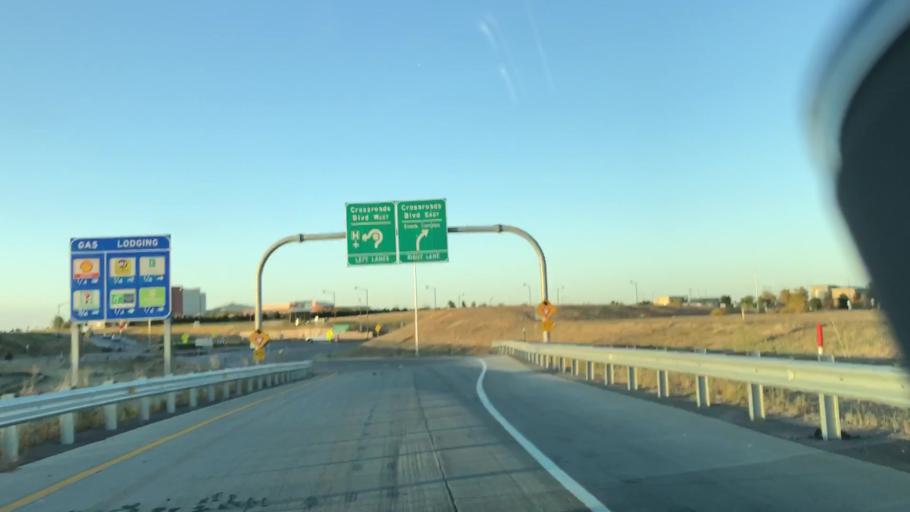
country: US
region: Colorado
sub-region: Larimer County
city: Loveland
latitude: 40.4345
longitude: -104.9916
